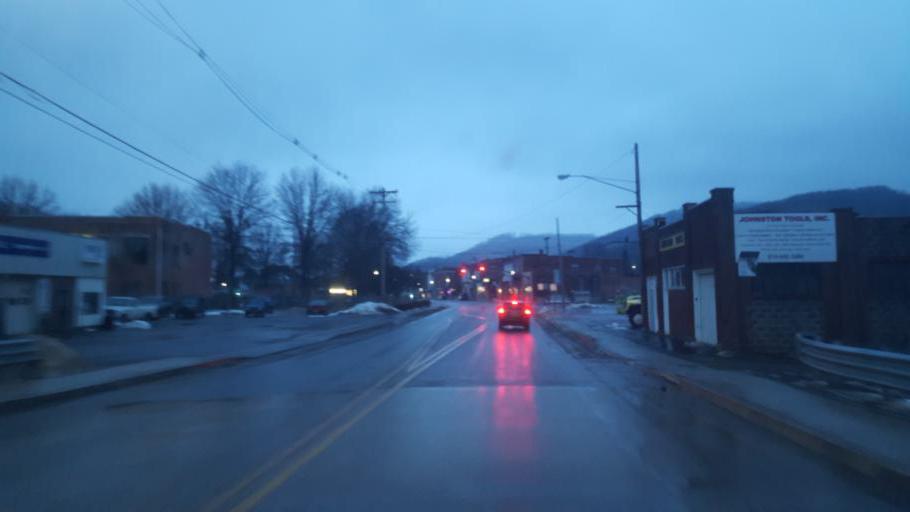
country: US
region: Pennsylvania
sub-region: McKean County
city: Port Allegany
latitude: 41.8099
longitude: -78.2797
